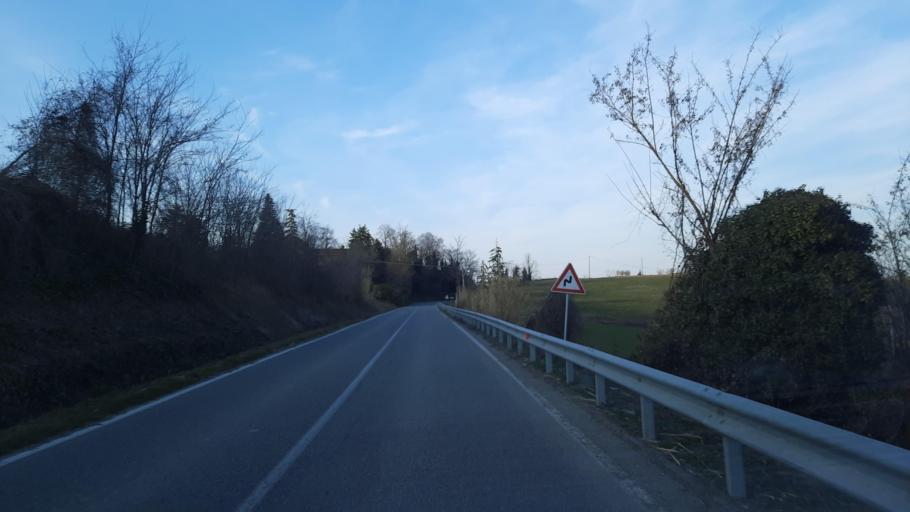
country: IT
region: Piedmont
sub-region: Provincia di Alessandria
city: Rosignano Monferrato
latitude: 45.0862
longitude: 8.4136
